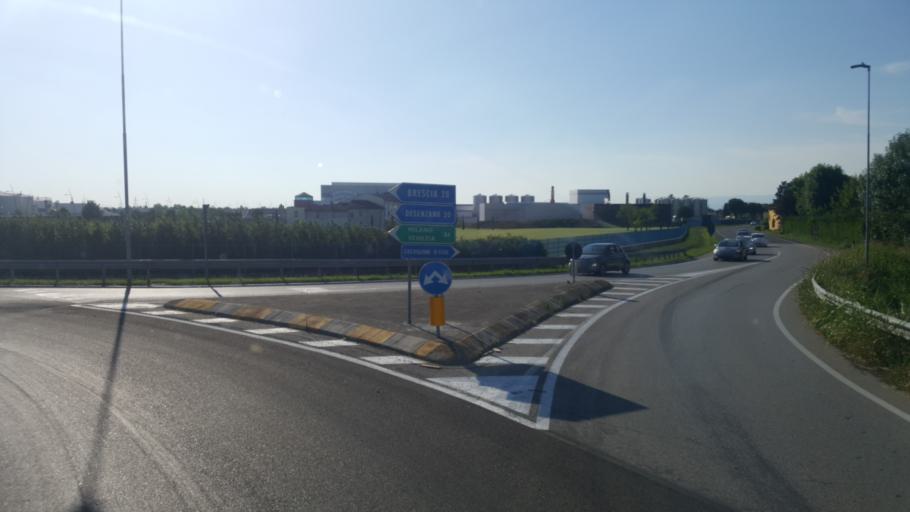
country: IT
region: Lombardy
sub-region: Provincia di Mantova
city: Castiglione delle Stiviere
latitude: 45.3650
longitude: 10.4949
